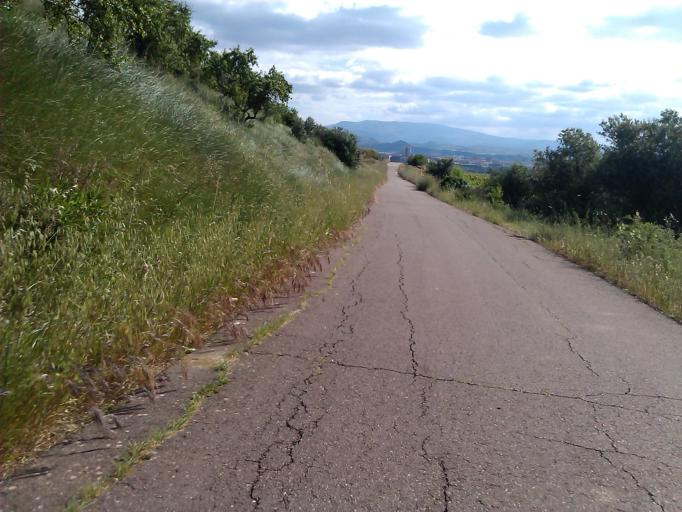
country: ES
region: Basque Country
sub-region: Provincia de Alava
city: Oyon
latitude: 42.4841
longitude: -2.4325
